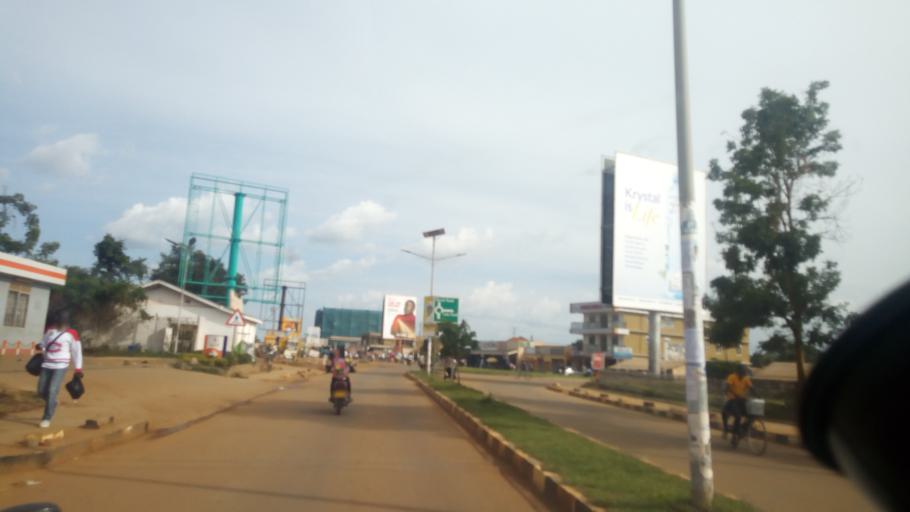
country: UG
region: Northern Region
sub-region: Lira District
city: Lira
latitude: 2.2344
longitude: 32.8932
